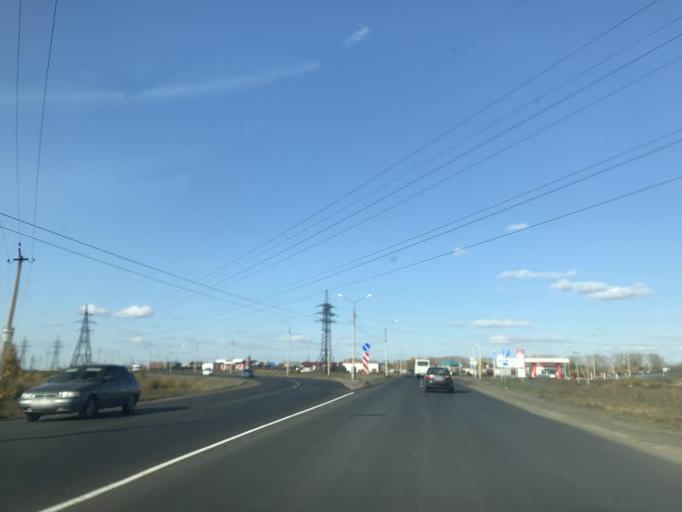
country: RU
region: Chelyabinsk
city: Roshchino
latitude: 55.2282
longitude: 61.2872
